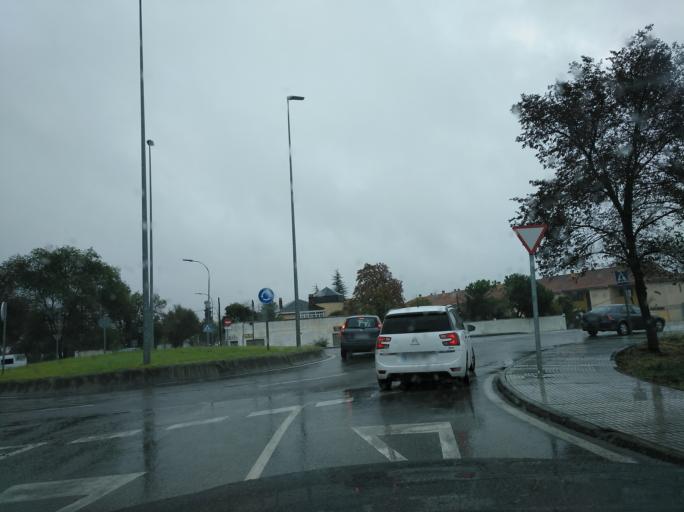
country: ES
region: Extremadura
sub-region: Provincia de Badajoz
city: Badajoz
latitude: 38.8866
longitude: -6.9895
